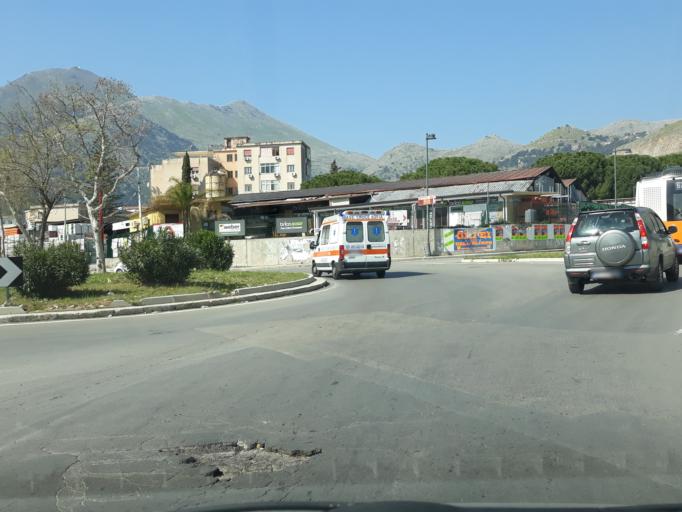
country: IT
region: Sicily
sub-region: Palermo
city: Palermo
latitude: 38.1310
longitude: 13.3041
